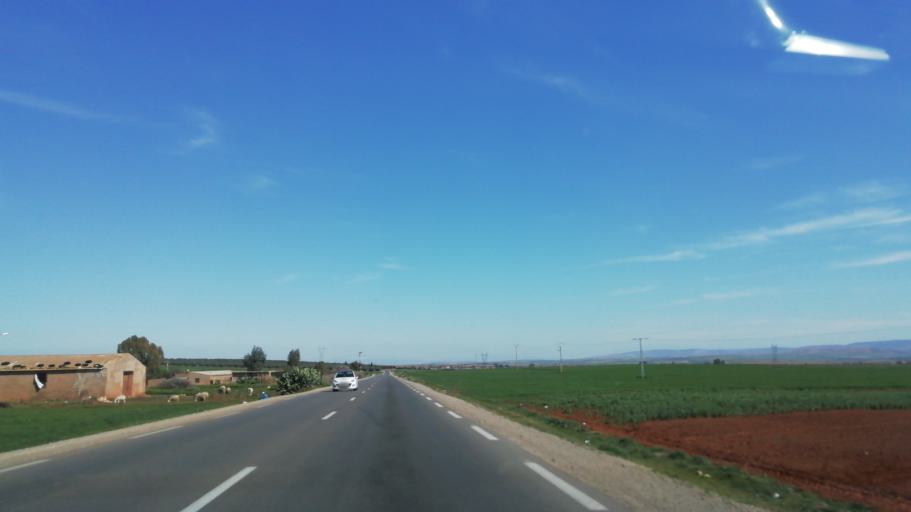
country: DZ
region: Mascara
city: Mascara
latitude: 35.4181
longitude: 0.4146
